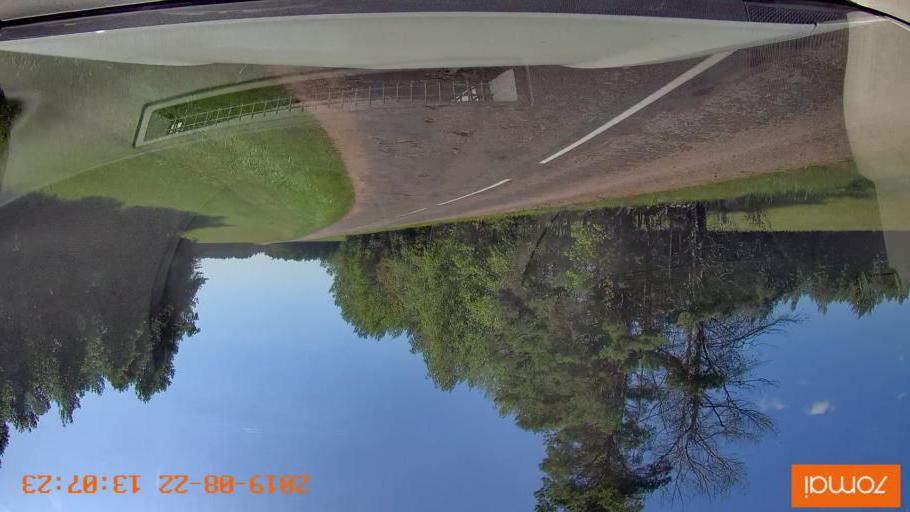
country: BY
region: Minsk
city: Prawdzinski
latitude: 53.3364
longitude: 27.8339
